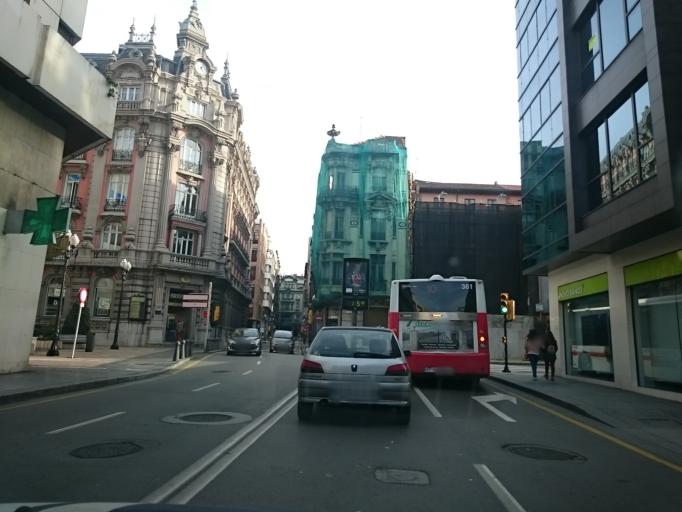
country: ES
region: Asturias
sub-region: Province of Asturias
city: Gijon
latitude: 43.5460
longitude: -5.6426
